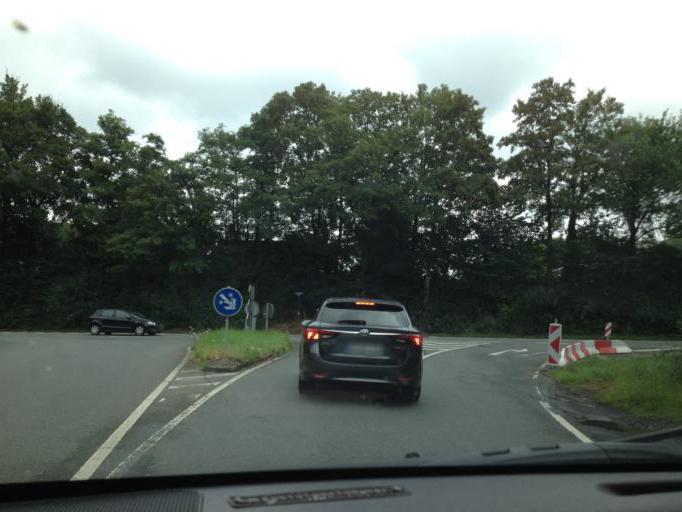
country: DE
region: North Rhine-Westphalia
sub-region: Regierungsbezirk Arnsberg
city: Unna
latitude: 51.5280
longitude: 7.6706
